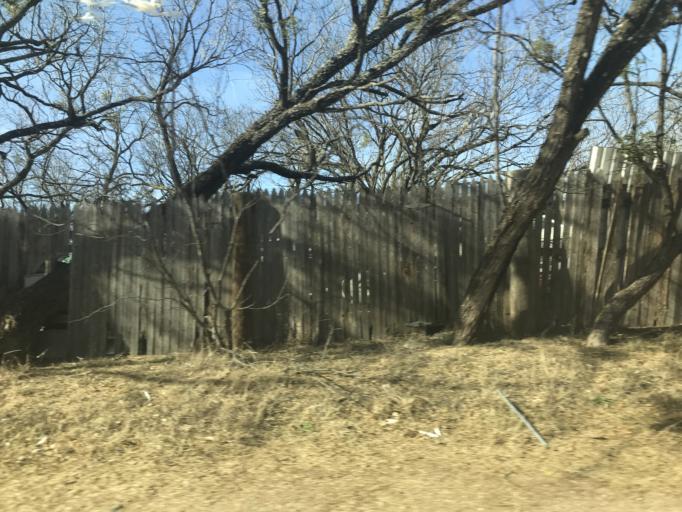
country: US
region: Texas
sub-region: Taylor County
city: Abilene
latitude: 32.4984
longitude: -99.7426
